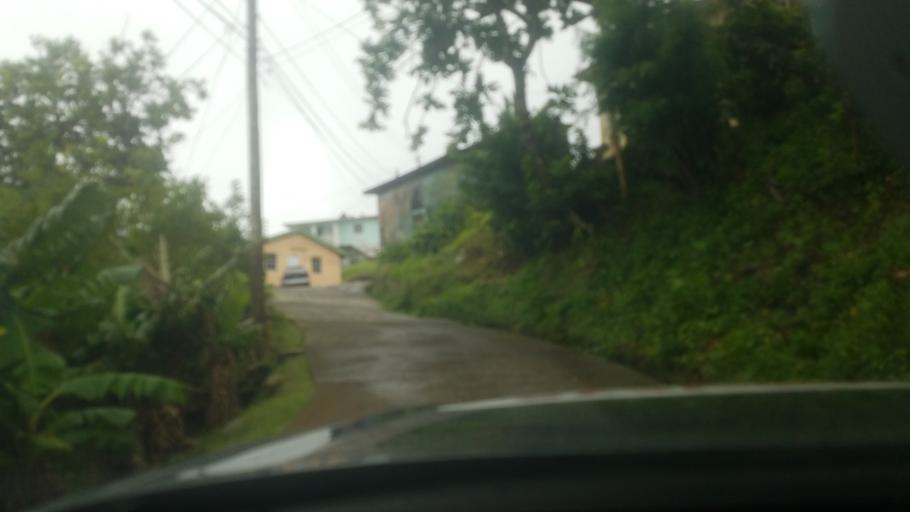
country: LC
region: Gros-Islet
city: Gros Islet
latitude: 14.0343
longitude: -60.9301
